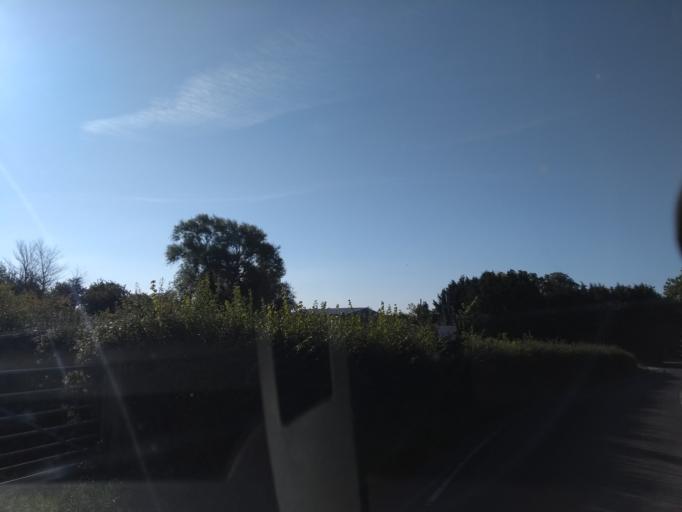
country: GB
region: England
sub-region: Somerset
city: Wedmore
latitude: 51.2446
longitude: -2.8265
